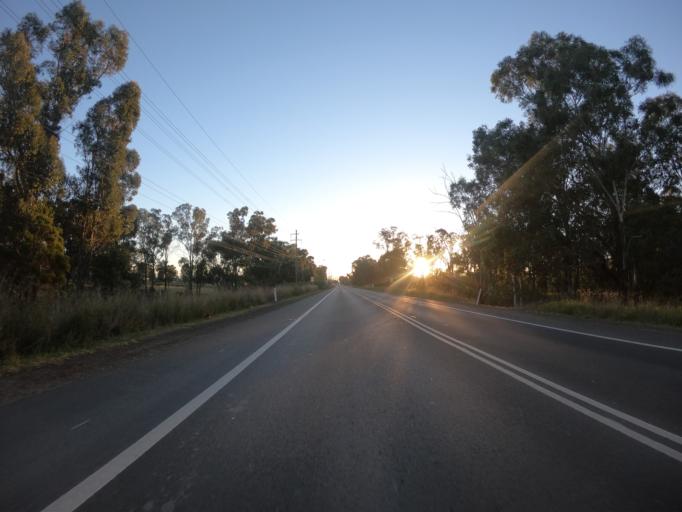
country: AU
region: New South Wales
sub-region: Hawkesbury
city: South Windsor
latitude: -33.6325
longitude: 150.7905
